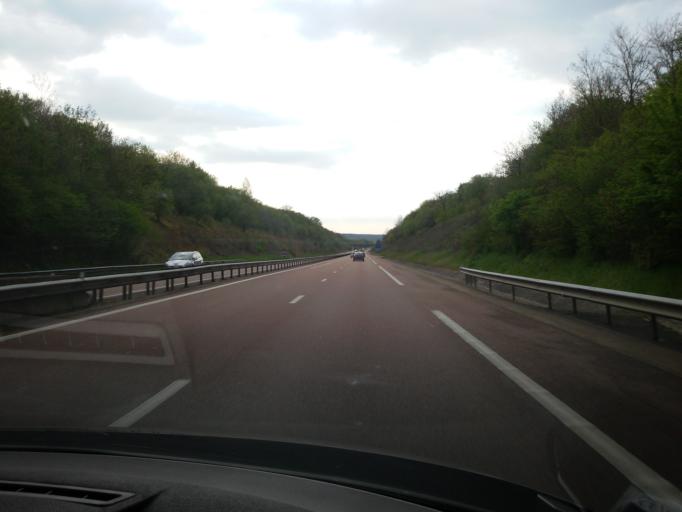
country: FR
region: Champagne-Ardenne
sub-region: Departement de la Haute-Marne
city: Chateauvillain
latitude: 48.0464
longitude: 4.9809
